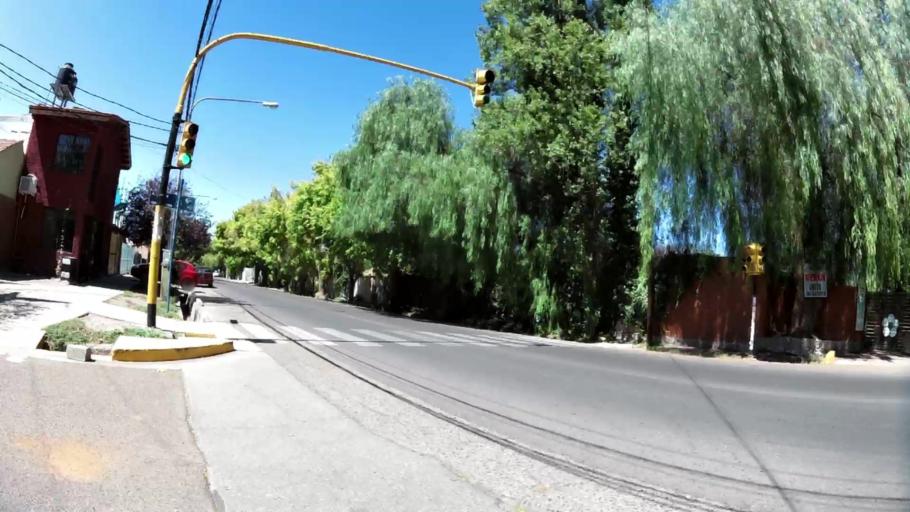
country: AR
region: Mendoza
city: Las Heras
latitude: -32.8528
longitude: -68.8533
